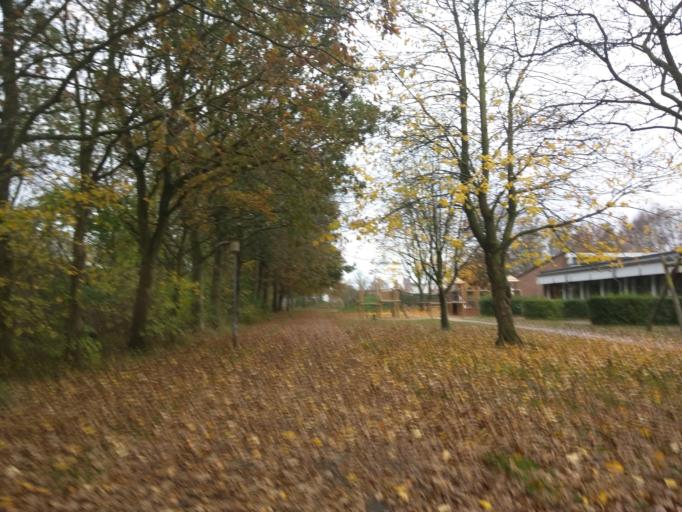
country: DK
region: Central Jutland
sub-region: Viborg Kommune
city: Viborg
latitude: 56.4651
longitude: 9.3898
